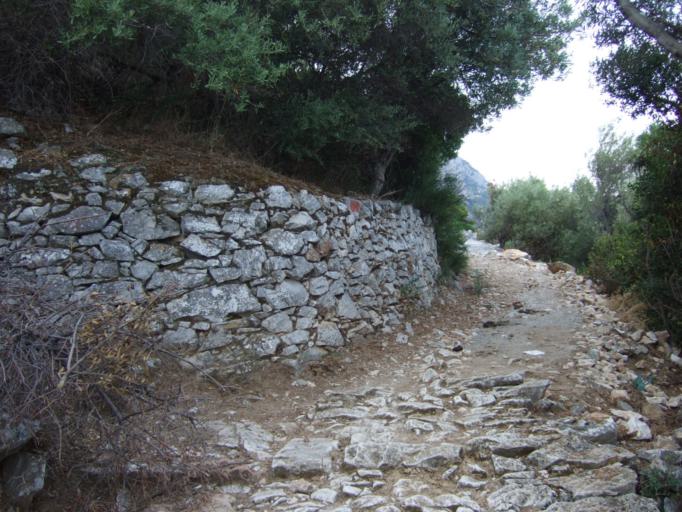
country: GR
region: Mount Athos
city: Karyes
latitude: 40.1426
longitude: 24.2943
